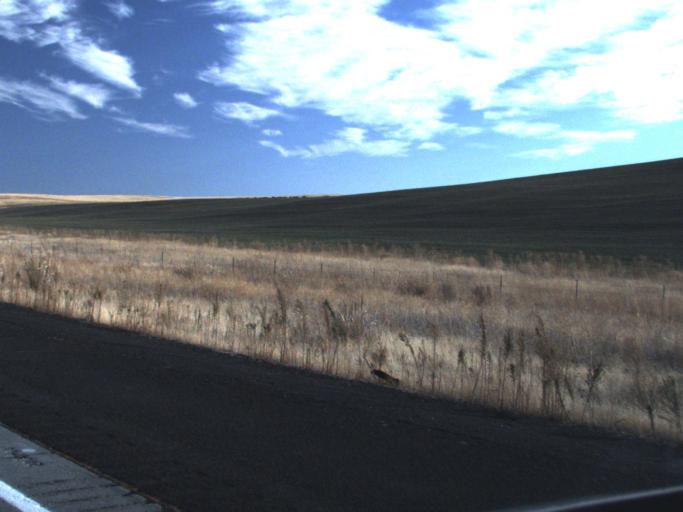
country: US
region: Washington
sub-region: Adams County
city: Ritzville
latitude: 47.0623
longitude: -118.4117
